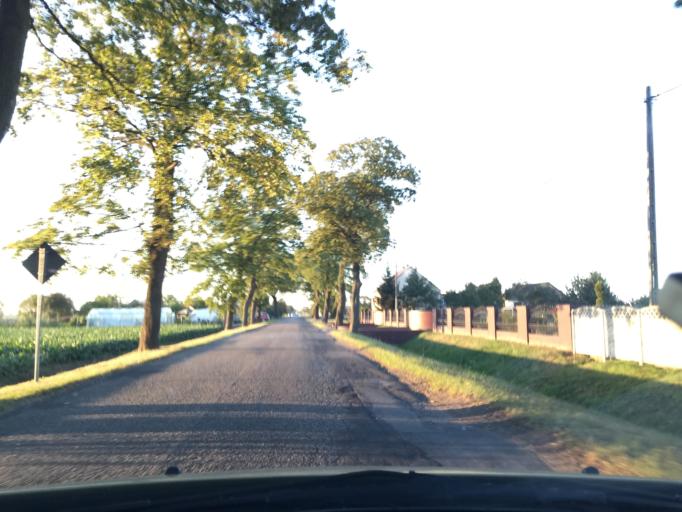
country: PL
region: Greater Poland Voivodeship
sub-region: Powiat pleszewski
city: Dobrzyca
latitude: 51.8212
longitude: 17.6207
